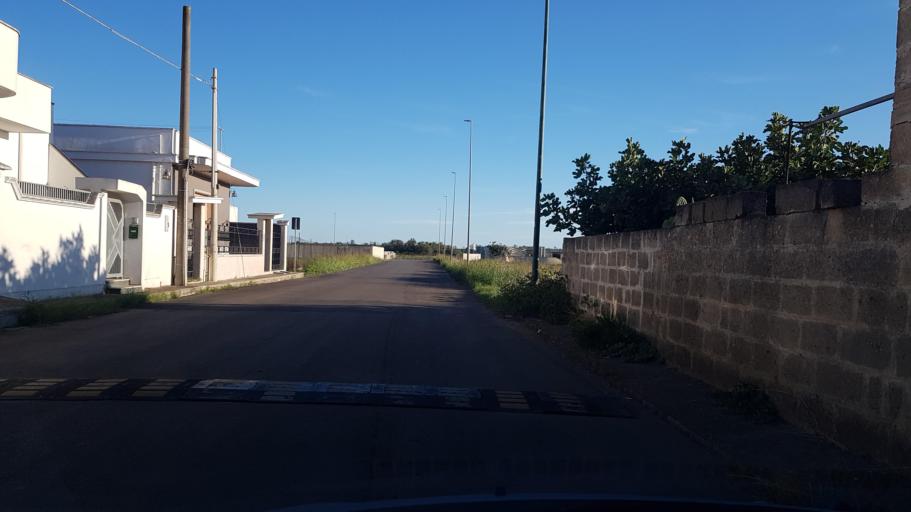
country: IT
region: Apulia
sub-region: Provincia di Brindisi
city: San Pancrazio Salentino
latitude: 40.4145
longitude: 17.8311
